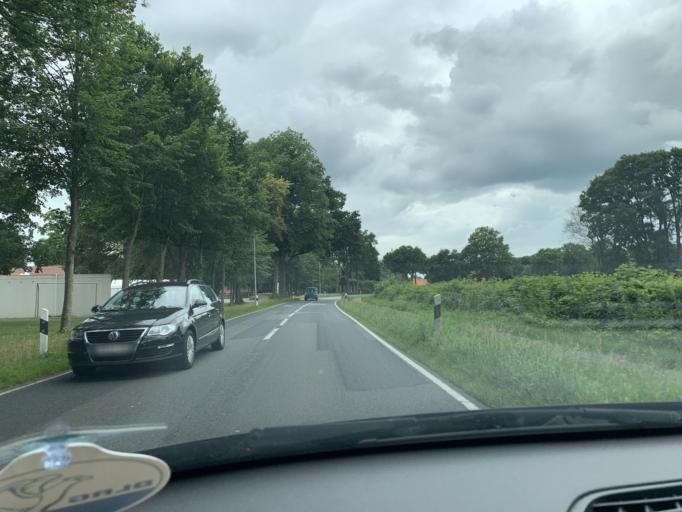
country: DE
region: Lower Saxony
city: Edewecht
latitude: 53.1286
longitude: 7.8976
